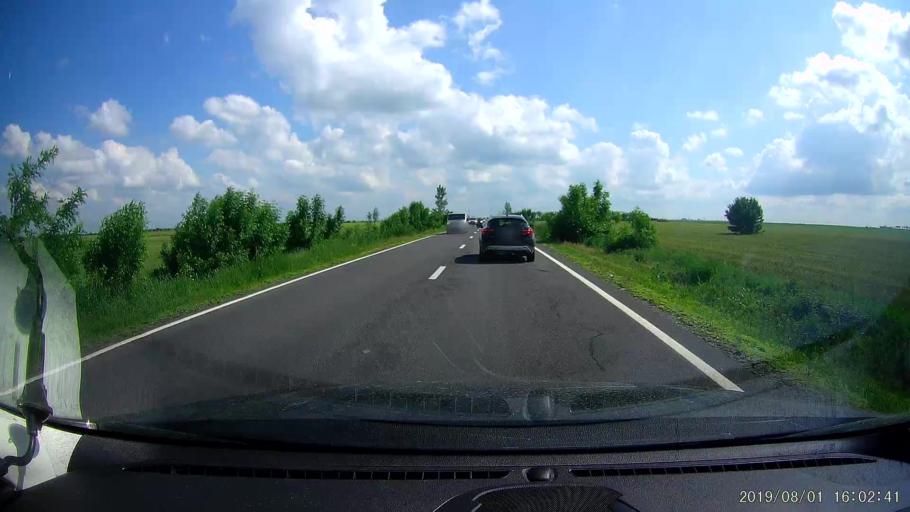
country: RO
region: Ialomita
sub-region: Comuna Ciulnita
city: Ciulnita
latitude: 44.4852
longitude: 27.3865
